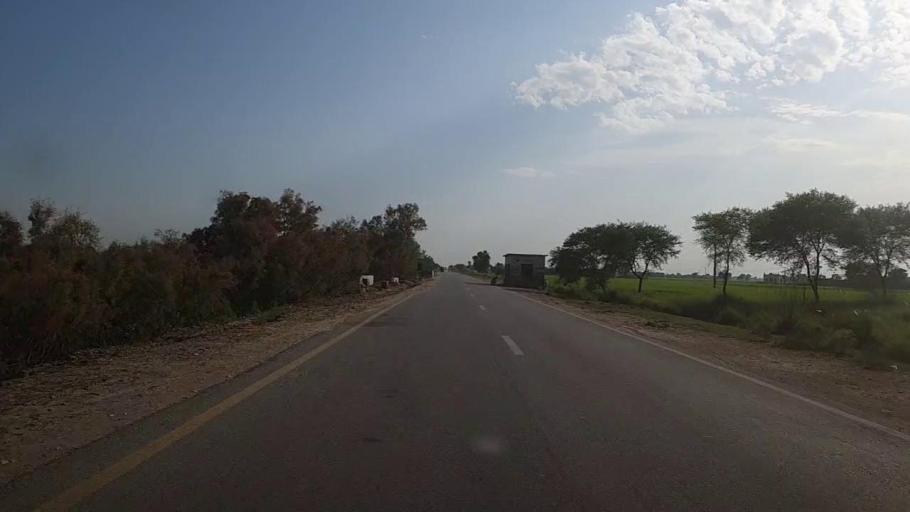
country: PK
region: Sindh
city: Thul
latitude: 28.2168
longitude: 68.7548
